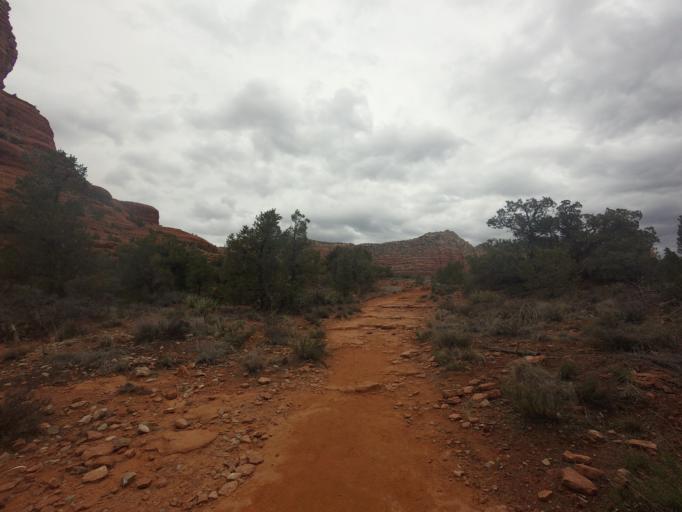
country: US
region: Arizona
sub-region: Yavapai County
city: Village of Oak Creek (Big Park)
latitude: 34.7981
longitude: -111.7494
